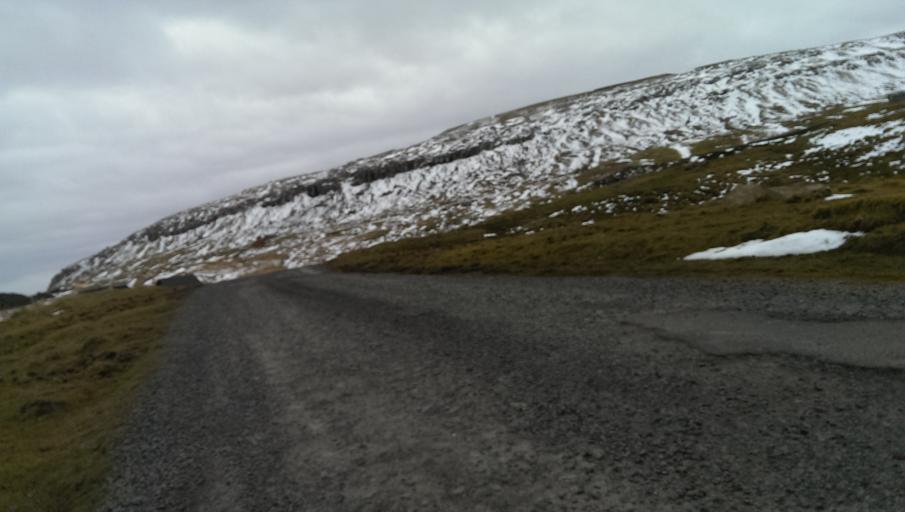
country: FO
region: Streymoy
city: Hoyvik
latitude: 62.0331
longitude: -6.8002
